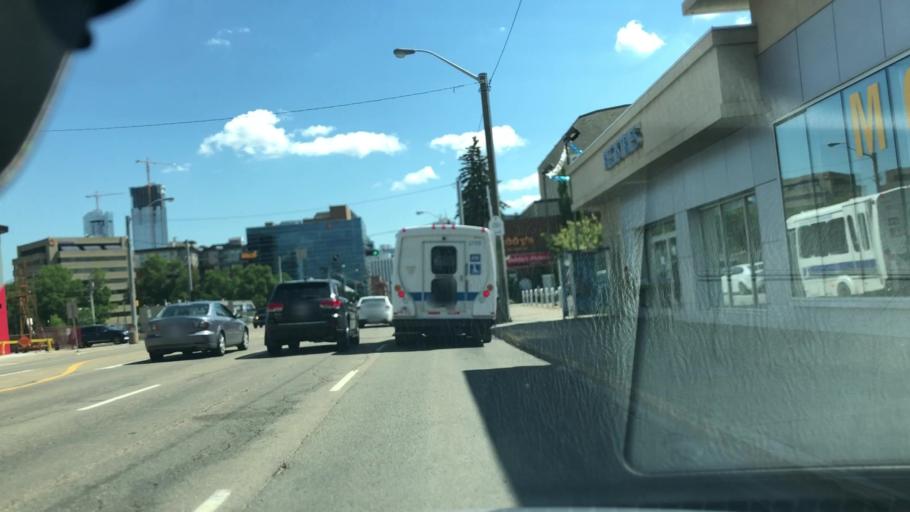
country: CA
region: Alberta
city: Edmonton
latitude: 53.5409
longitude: -113.5187
